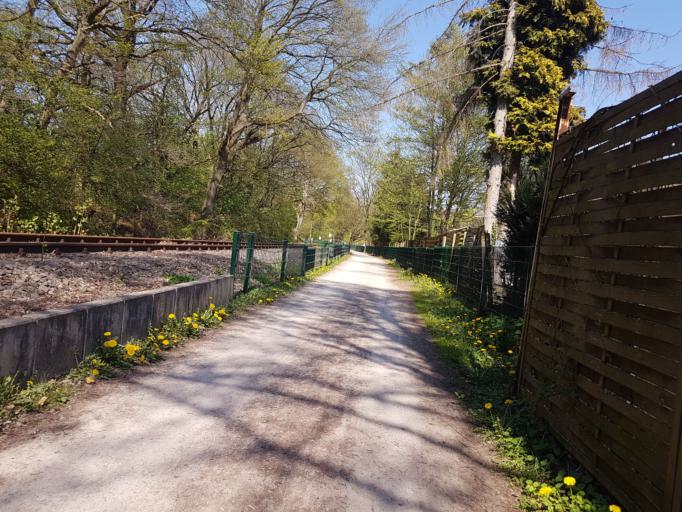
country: DE
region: North Rhine-Westphalia
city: Witten
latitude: 51.4173
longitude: 7.3484
